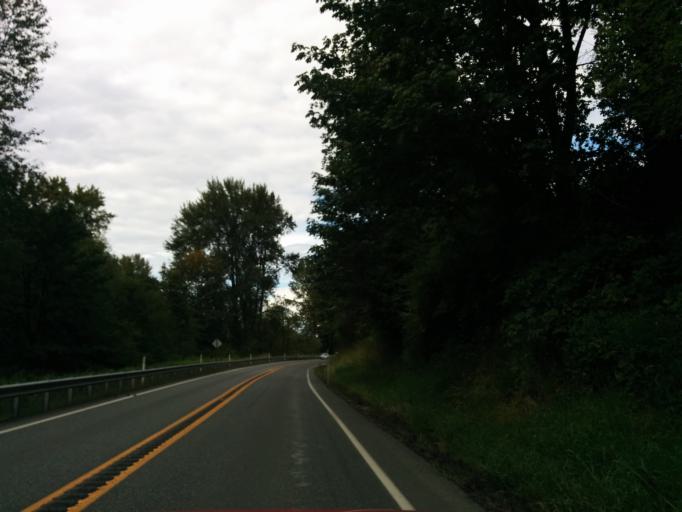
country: US
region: Washington
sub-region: King County
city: Duvall
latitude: 47.7481
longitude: -121.9859
